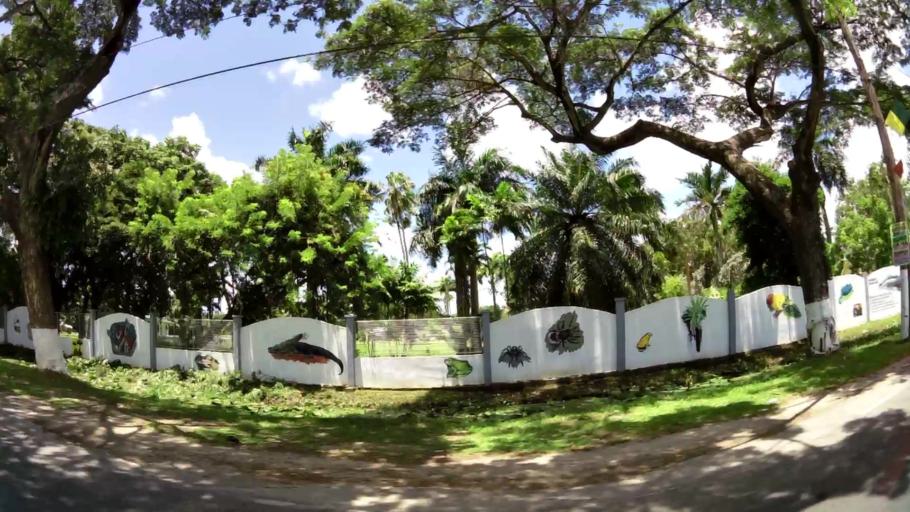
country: GY
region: Demerara-Mahaica
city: Georgetown
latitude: 6.8073
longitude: -58.1484
